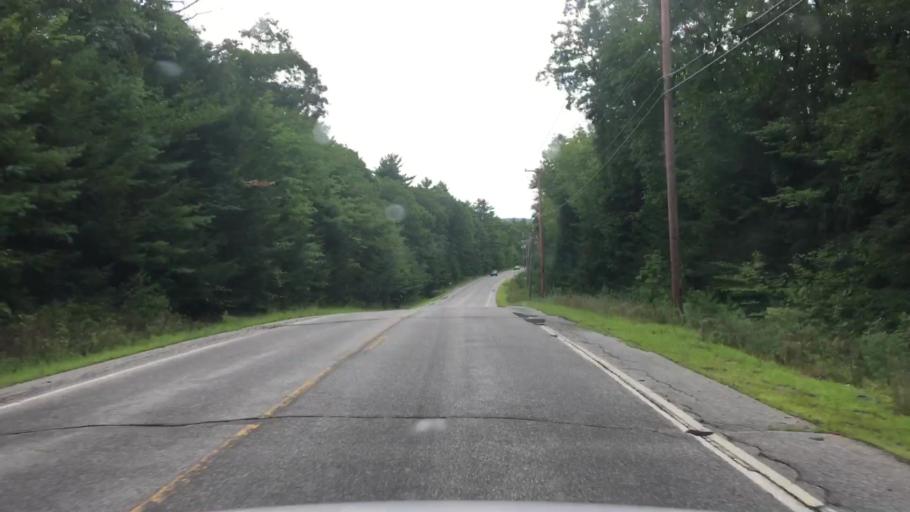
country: US
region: Maine
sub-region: York County
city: Cornish
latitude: 43.8156
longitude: -70.7766
